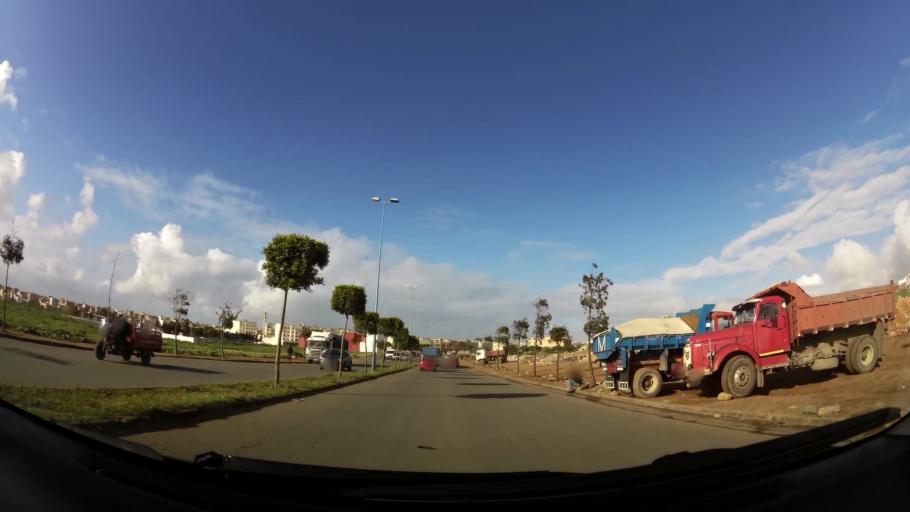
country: MA
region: Grand Casablanca
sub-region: Casablanca
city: Casablanca
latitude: 33.5610
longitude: -7.6849
